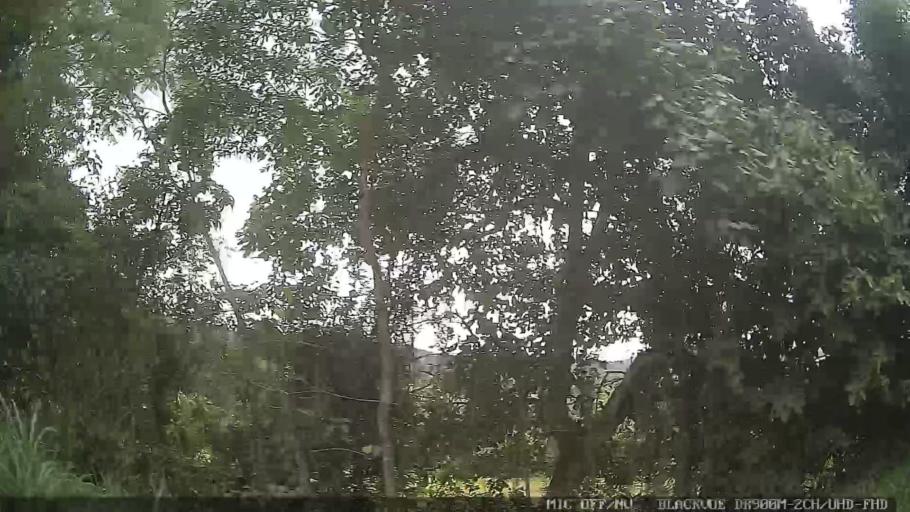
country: BR
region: Sao Paulo
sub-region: Ferraz De Vasconcelos
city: Ferraz de Vasconcelos
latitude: -23.6224
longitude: -46.3868
